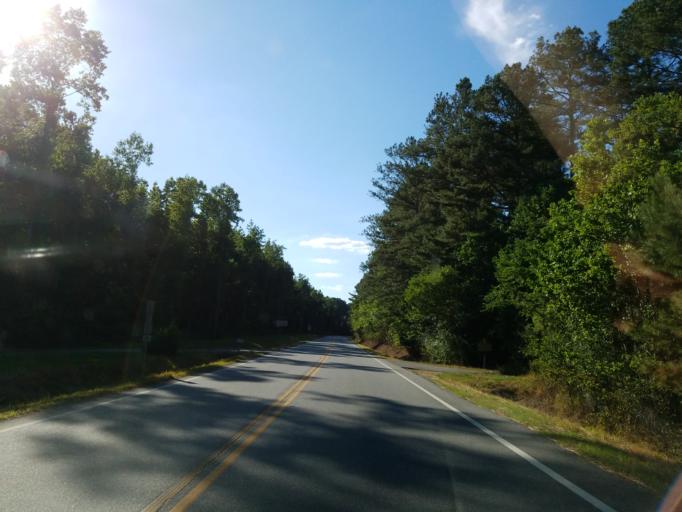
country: US
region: Georgia
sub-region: Gordon County
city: Calhoun
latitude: 34.6087
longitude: -85.0458
